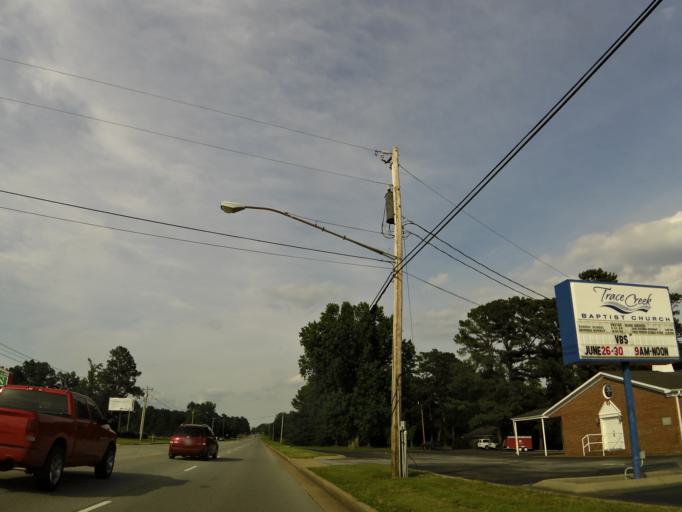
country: US
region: Tennessee
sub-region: Humphreys County
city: Johnsonville
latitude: 36.0348
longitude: -87.9398
